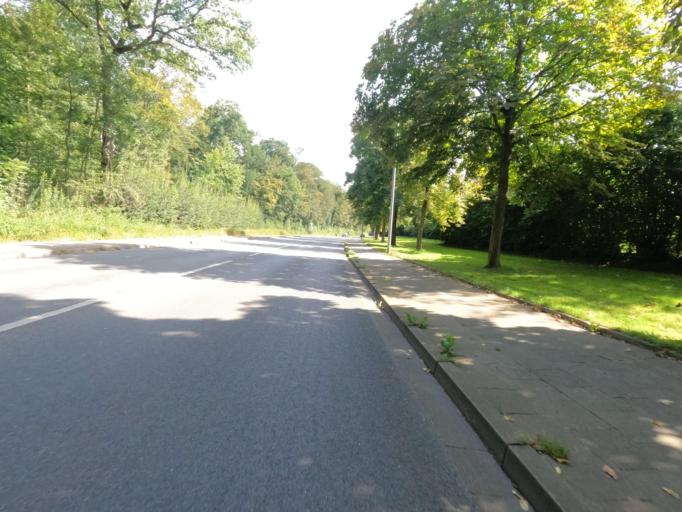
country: DE
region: North Rhine-Westphalia
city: Geilenkirchen
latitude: 50.9731
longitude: 6.1267
